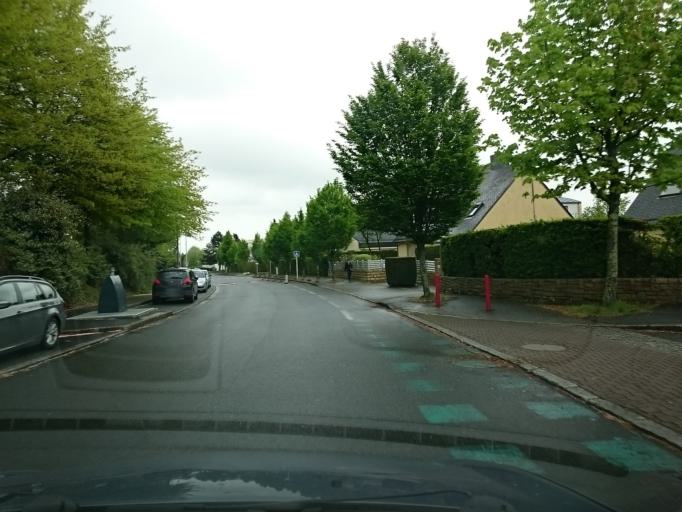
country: FR
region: Brittany
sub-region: Departement d'Ille-et-Vilaine
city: Saint-Gregoire
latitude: 48.1442
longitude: -1.6836
